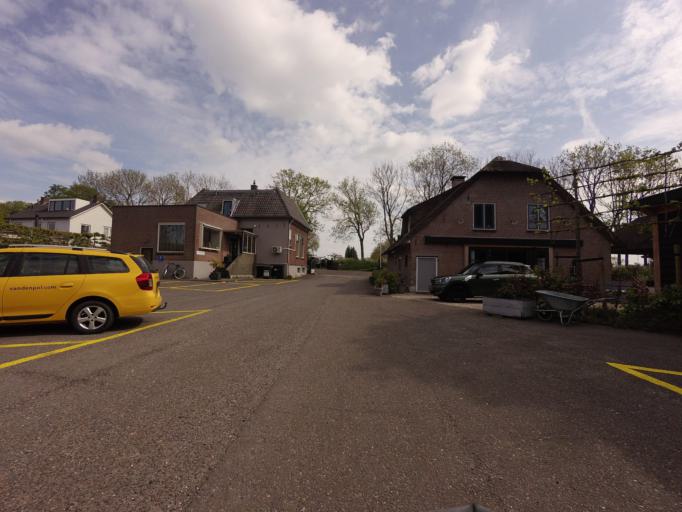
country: NL
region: Utrecht
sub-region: Gemeente Oudewater
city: Oudewater
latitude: 52.0240
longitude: 4.8607
